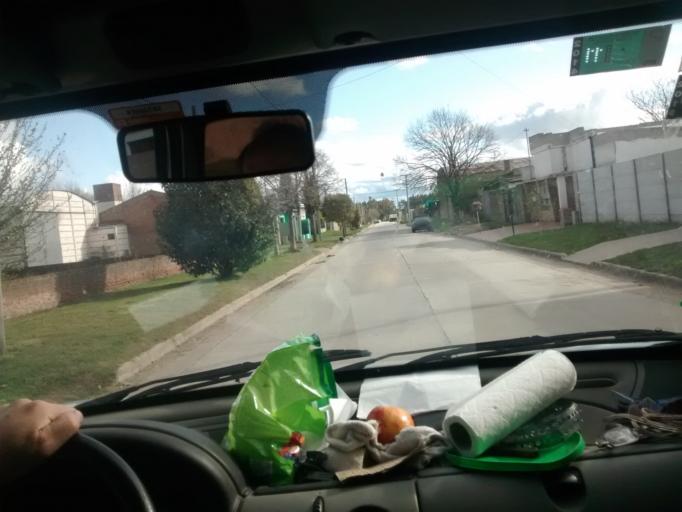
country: AR
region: Buenos Aires
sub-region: Partido de Loberia
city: Loberia
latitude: -38.1711
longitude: -58.7757
